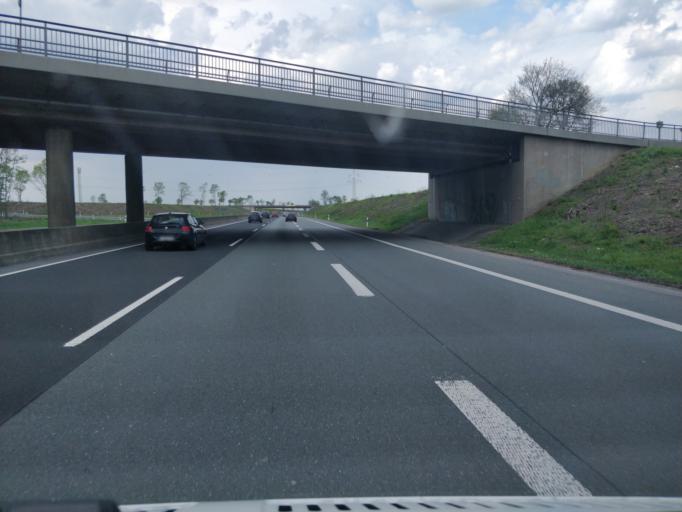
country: DE
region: North Rhine-Westphalia
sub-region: Regierungsbezirk Koln
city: Euskirchen
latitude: 50.6478
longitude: 6.7223
